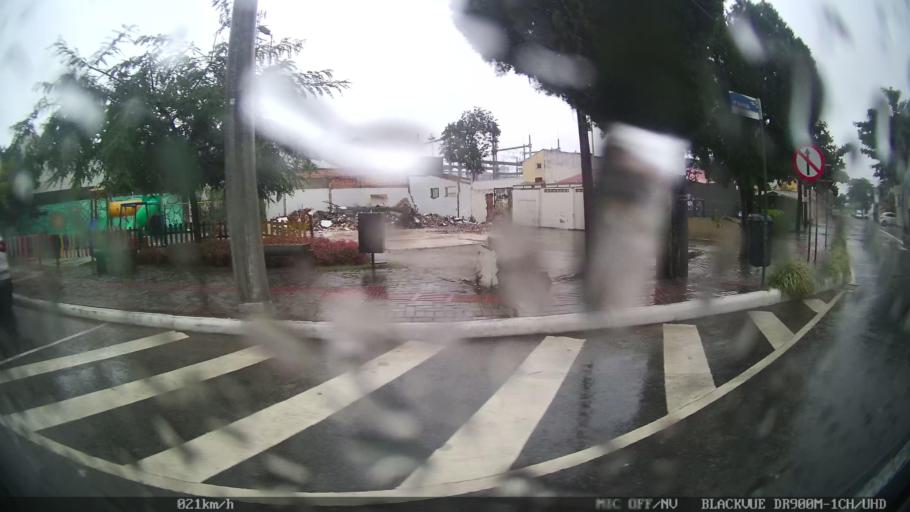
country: BR
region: Santa Catarina
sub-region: Balneario Camboriu
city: Balneario Camboriu
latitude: -27.0011
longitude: -48.6338
